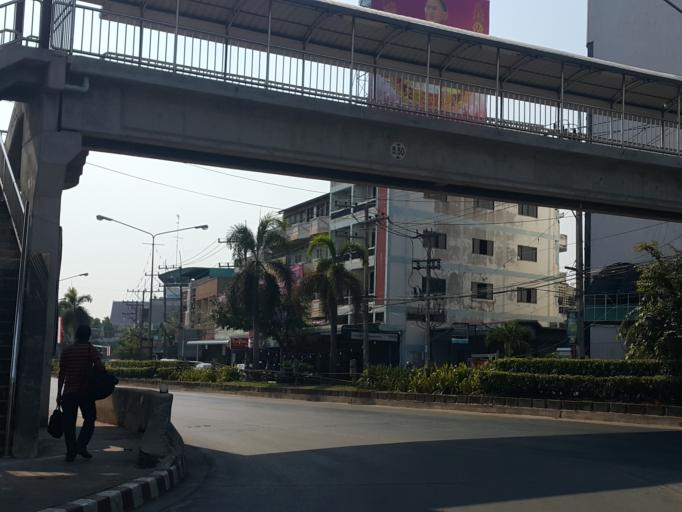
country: TH
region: Phitsanulok
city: Phitsanulok
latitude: 16.8209
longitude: 100.2645
